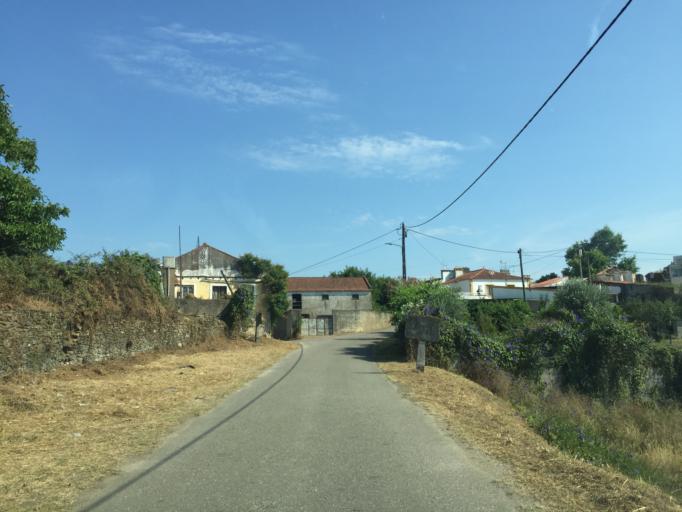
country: PT
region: Santarem
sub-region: Constancia
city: Constancia
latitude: 39.5715
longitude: -8.2937
